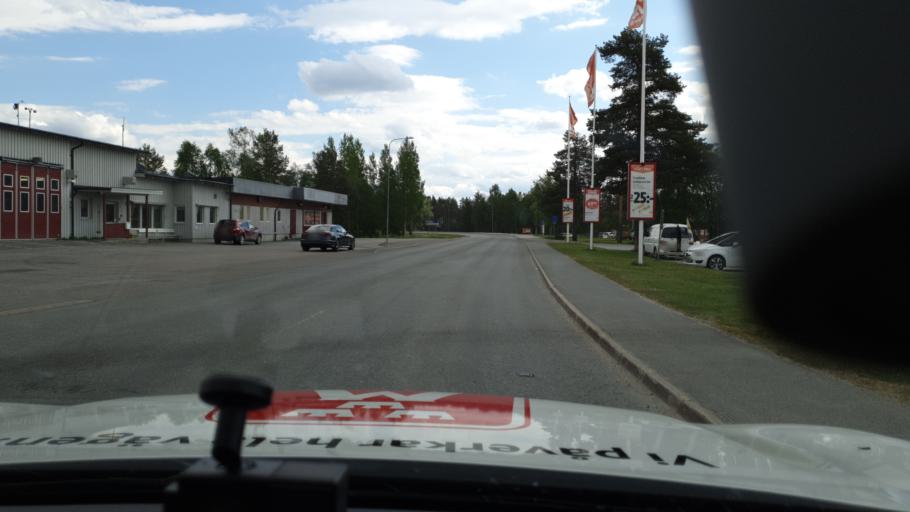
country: SE
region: Vaesterbotten
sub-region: Sorsele Kommun
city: Sorsele
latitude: 65.5369
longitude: 17.5306
